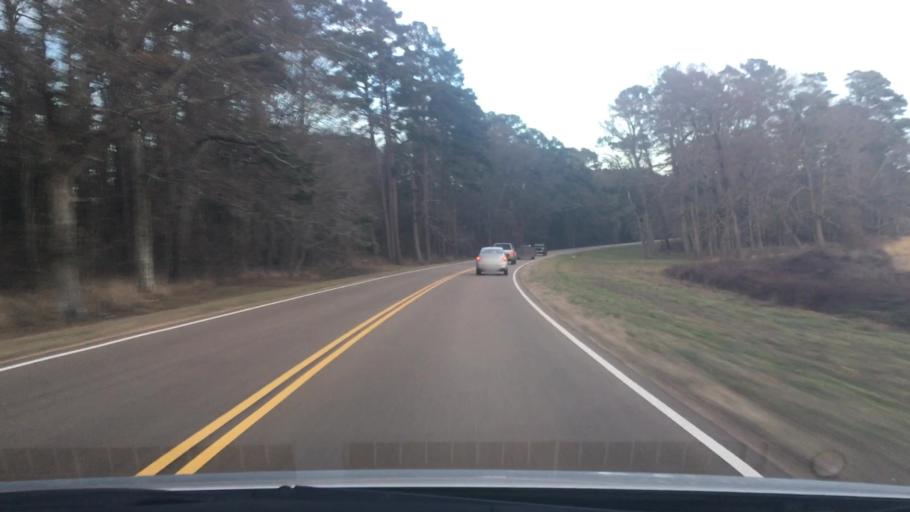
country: US
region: Mississippi
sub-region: Madison County
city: Canton
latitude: 32.5143
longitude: -89.9923
